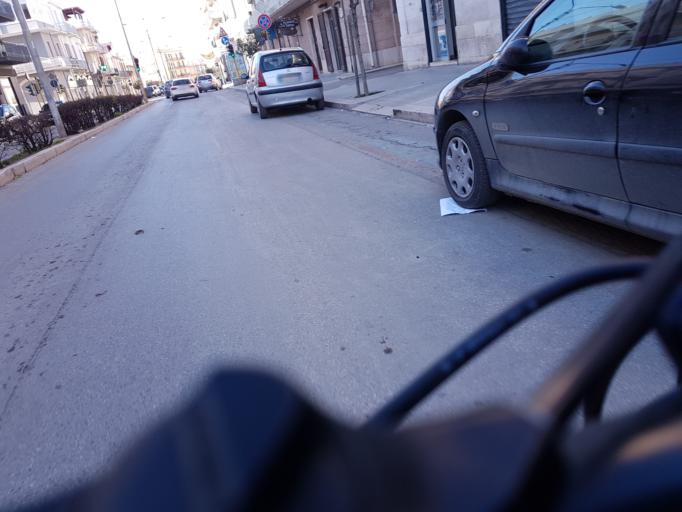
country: IT
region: Apulia
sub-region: Provincia di Bari
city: Corato
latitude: 41.1533
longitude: 16.4074
